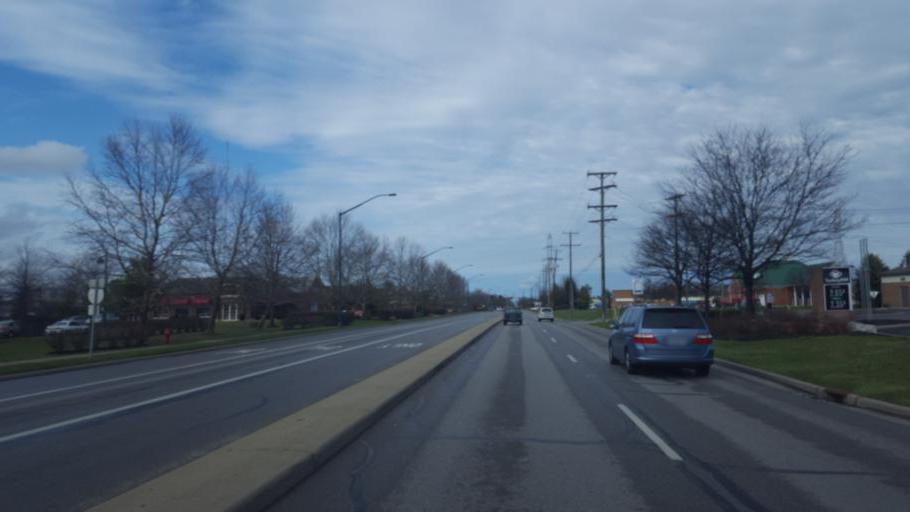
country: US
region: Ohio
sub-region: Franklin County
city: Westerville
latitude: 40.1474
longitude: -82.9235
